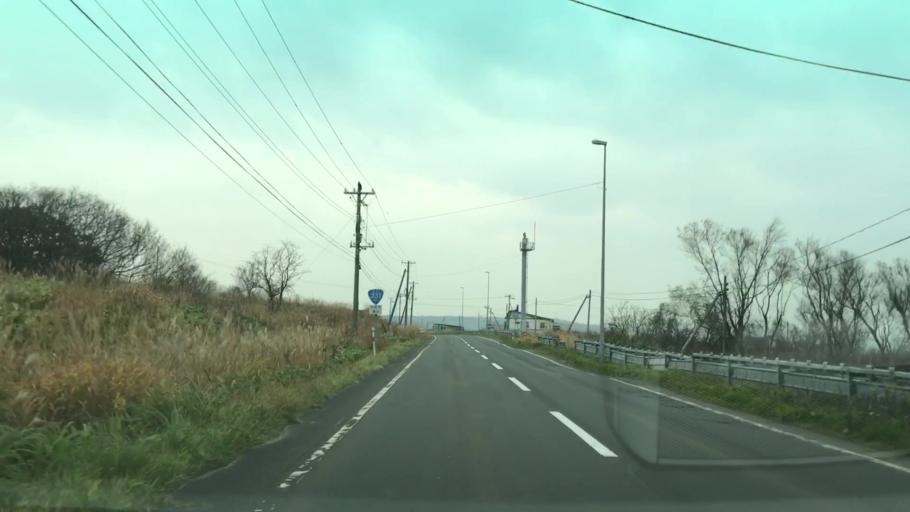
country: JP
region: Hokkaido
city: Ishikari
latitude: 43.3445
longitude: 141.4238
